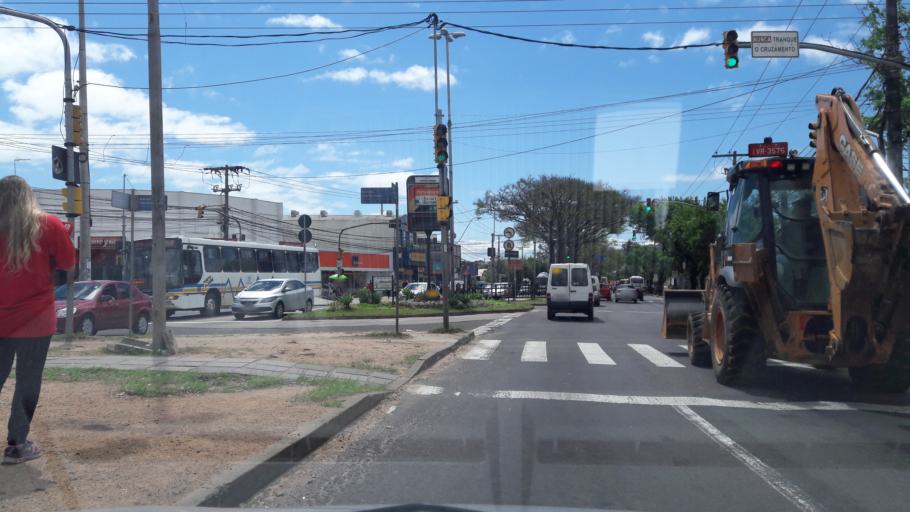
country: BR
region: Rio Grande do Sul
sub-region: Porto Alegre
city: Porto Alegre
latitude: -30.1024
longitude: -51.2310
